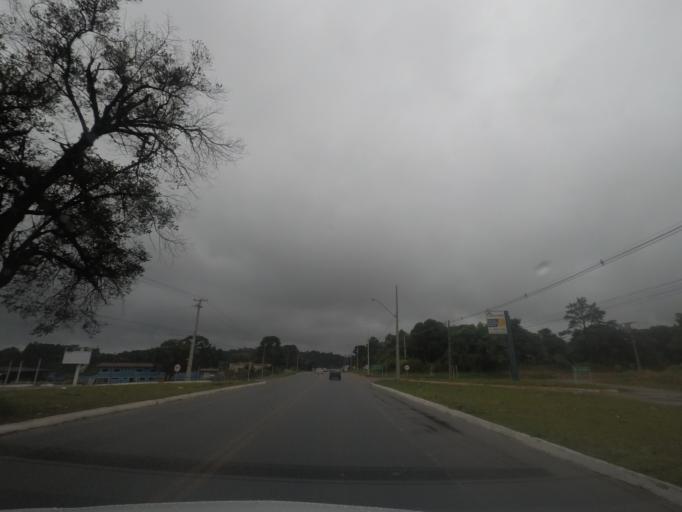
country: BR
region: Parana
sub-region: Colombo
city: Colombo
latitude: -25.3434
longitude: -49.1591
